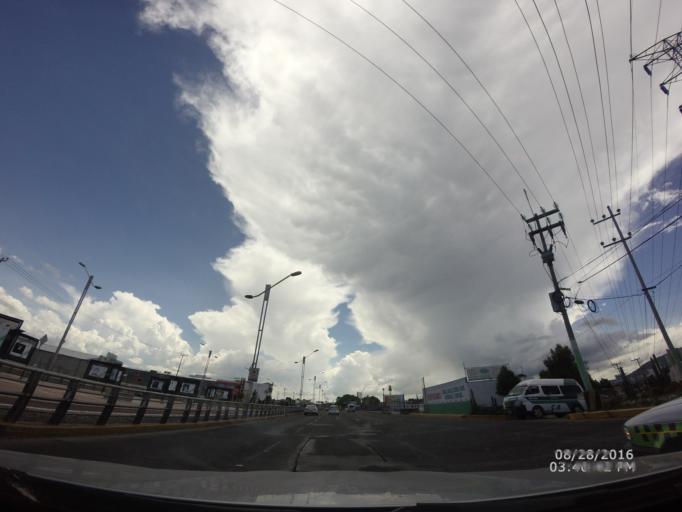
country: MX
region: Hidalgo
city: Pachuca de Soto
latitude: 20.1129
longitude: -98.7447
